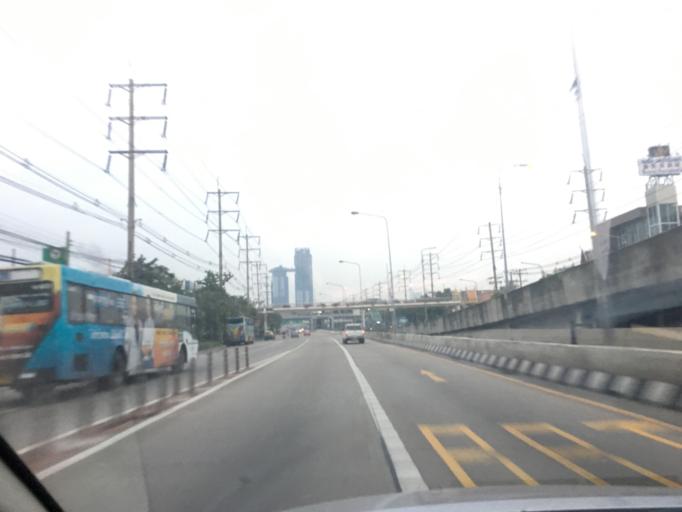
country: TH
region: Bangkok
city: Rat Burana
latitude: 13.6810
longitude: 100.5272
